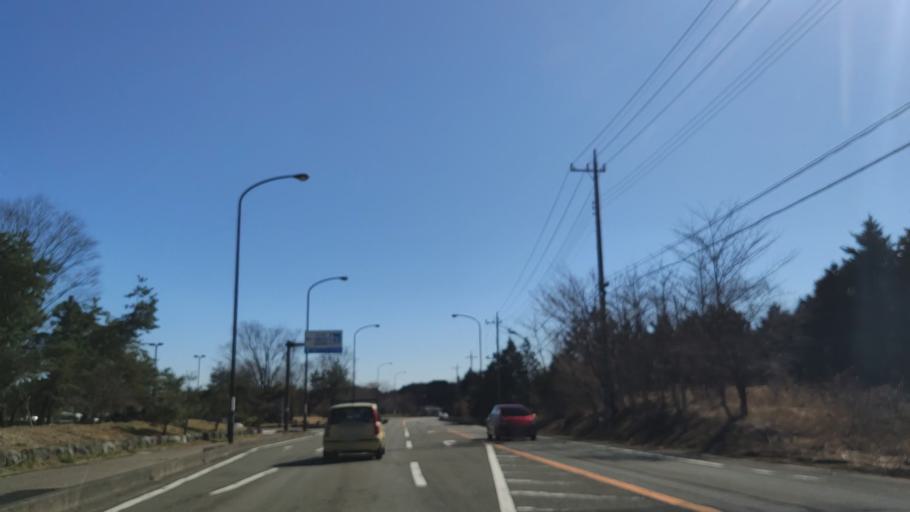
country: JP
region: Yamanashi
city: Fujikawaguchiko
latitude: 35.4150
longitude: 138.5902
